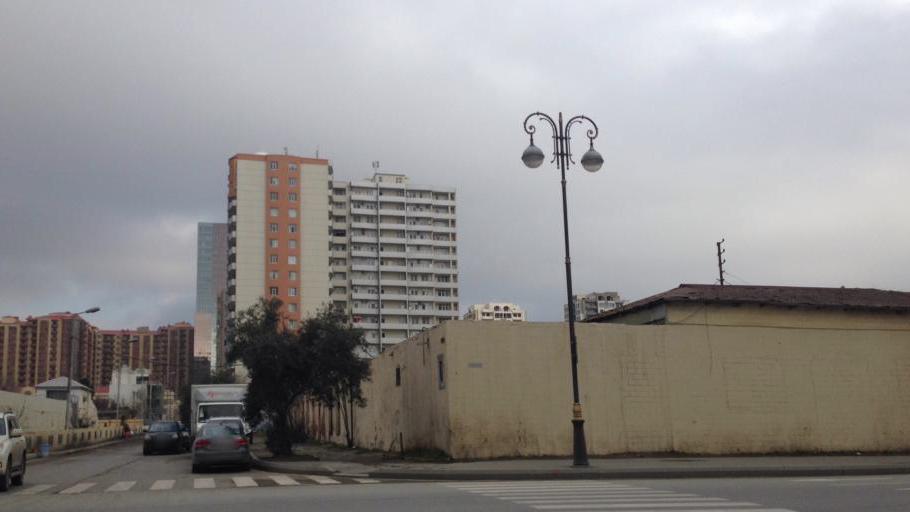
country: AZ
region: Baki
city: Baku
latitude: 40.3784
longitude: 49.8724
